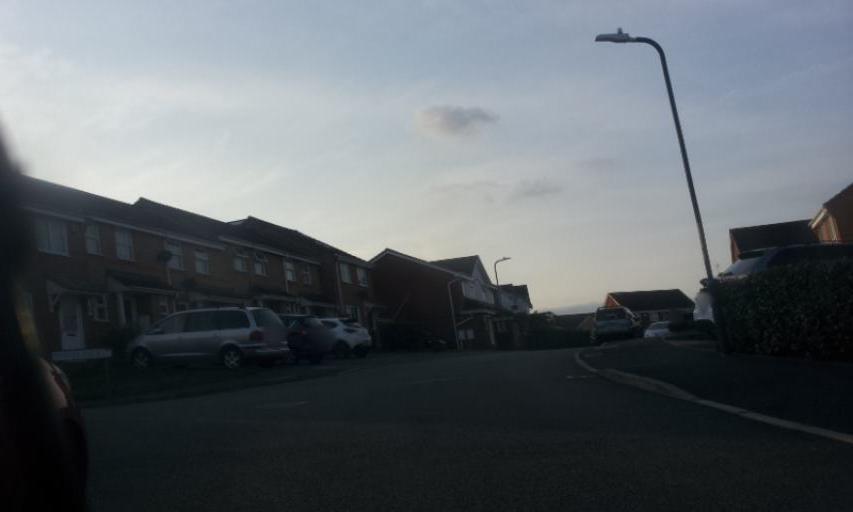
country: GB
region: England
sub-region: Kent
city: Maidstone
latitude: 51.2870
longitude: 0.5064
